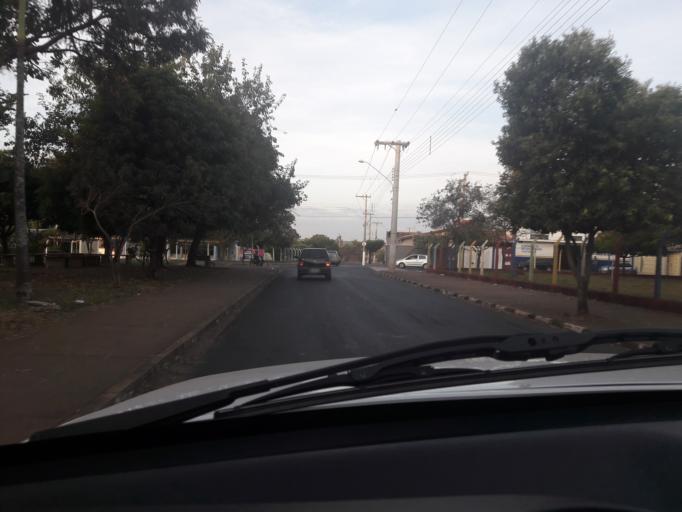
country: BR
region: Sao Paulo
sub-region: Moji-Guacu
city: Mogi-Gaucu
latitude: -22.3457
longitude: -46.9357
